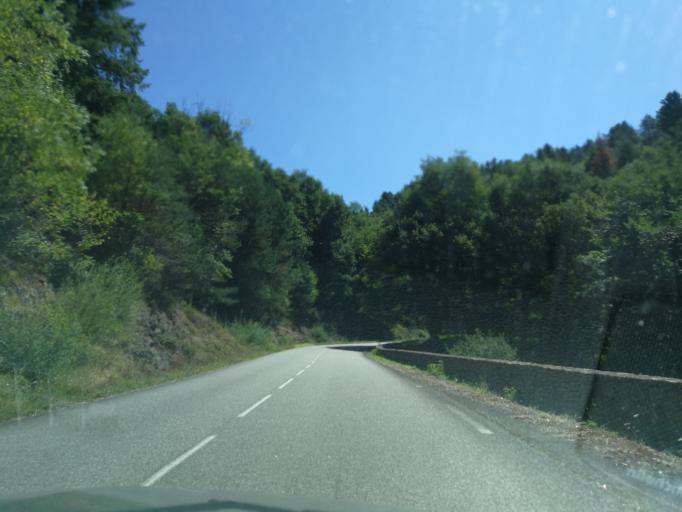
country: FR
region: Limousin
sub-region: Departement de la Correze
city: Argentat
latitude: 45.0752
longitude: 1.9457
